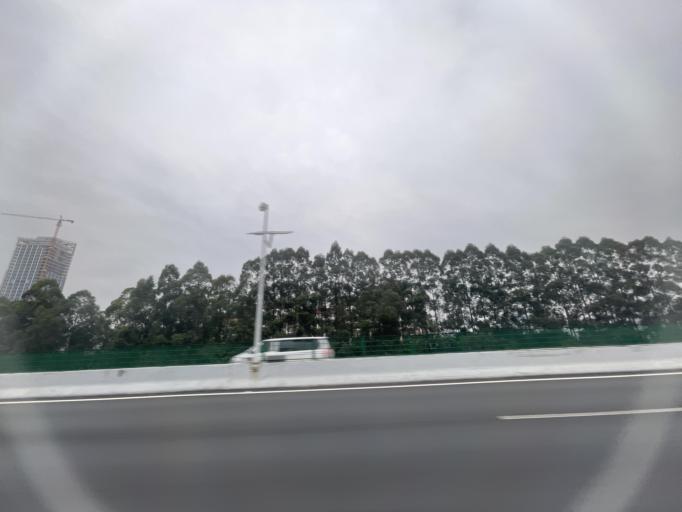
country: CN
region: Guangdong
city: Huangge
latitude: 22.7891
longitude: 113.5176
